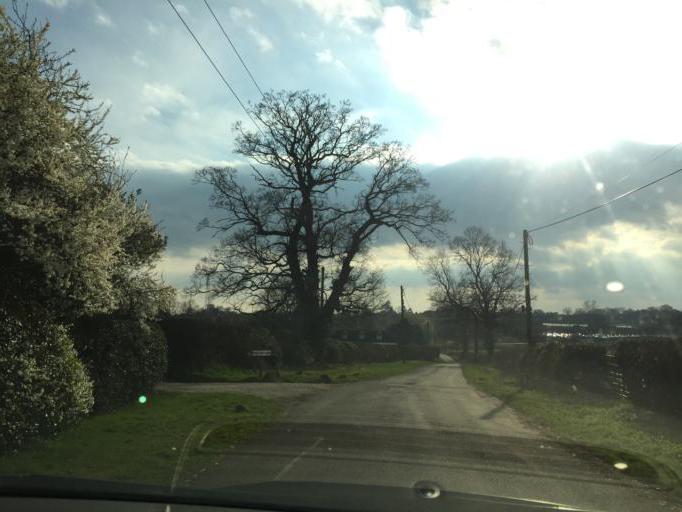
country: GB
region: England
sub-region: Solihull
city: Meriden
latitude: 52.4331
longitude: -1.5889
